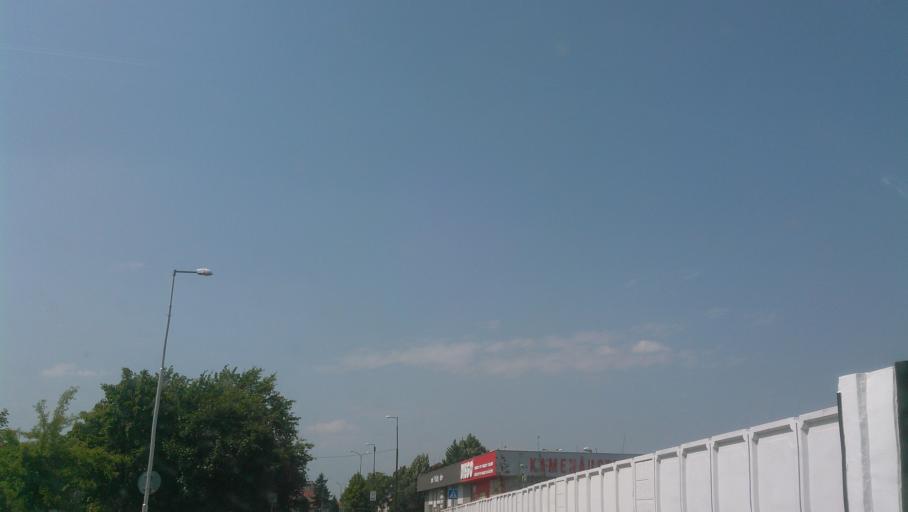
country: SK
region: Trnavsky
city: Dunajska Streda
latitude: 47.9999
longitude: 17.6231
